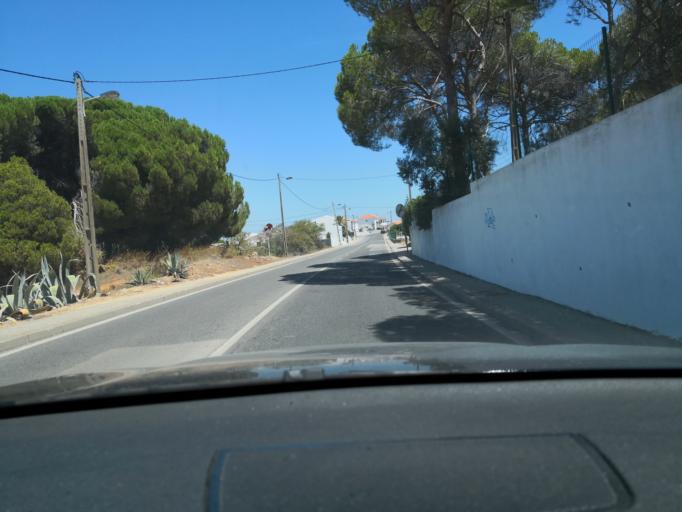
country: PT
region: Faro
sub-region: Albufeira
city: Ferreiras
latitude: 37.1051
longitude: -8.2146
